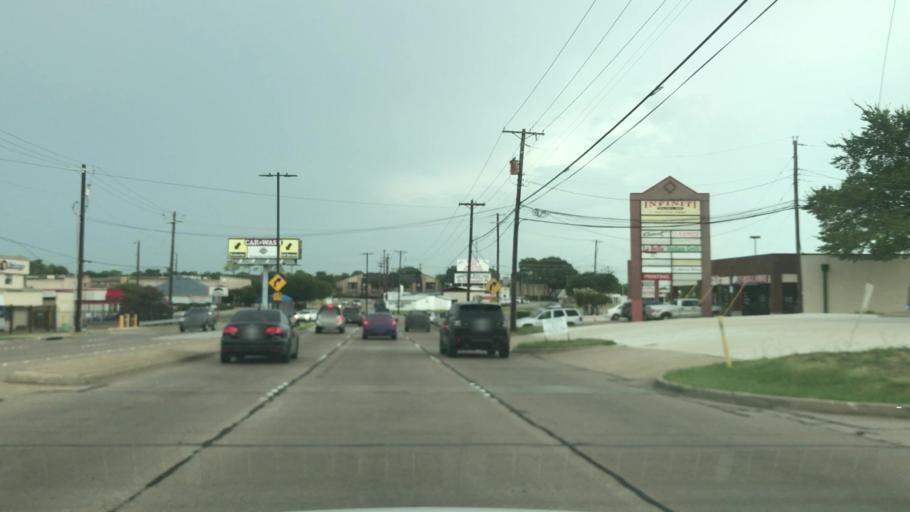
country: US
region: Texas
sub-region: Dallas County
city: Rowlett
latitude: 32.8641
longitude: -96.6047
